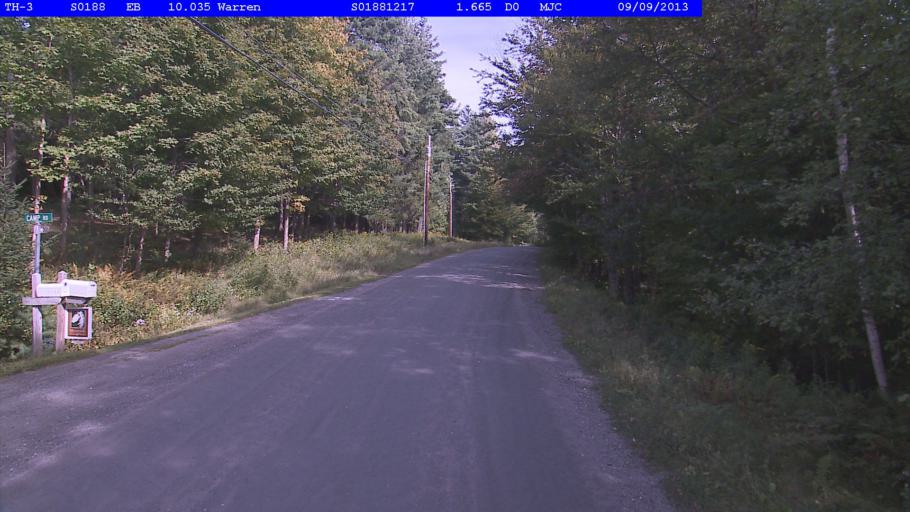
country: US
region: Vermont
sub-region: Addison County
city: Bristol
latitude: 44.1008
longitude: -72.8987
